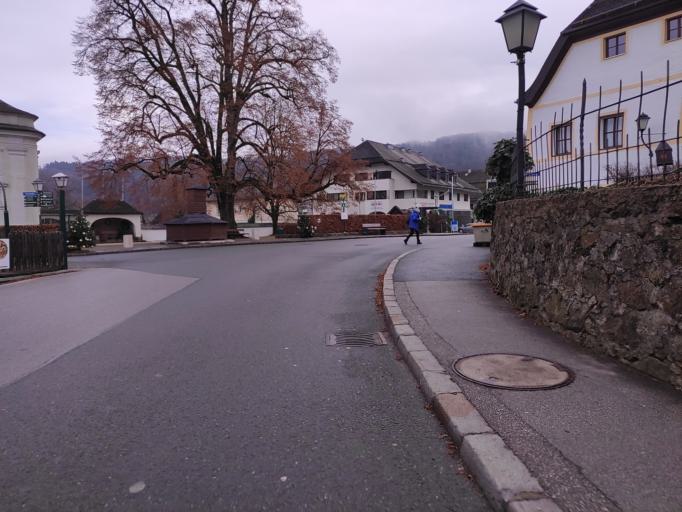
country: AT
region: Salzburg
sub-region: Politischer Bezirk Salzburg-Umgebung
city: Mattsee
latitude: 47.9707
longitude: 13.1044
